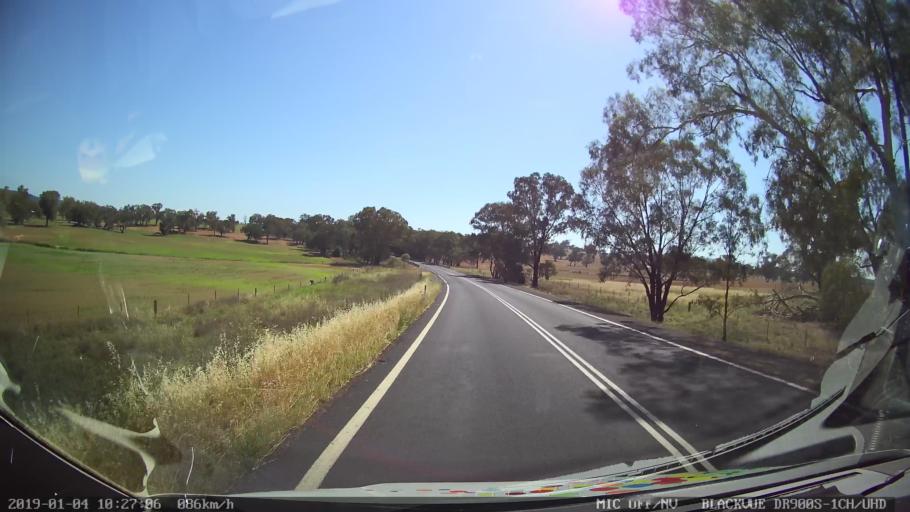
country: AU
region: New South Wales
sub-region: Cabonne
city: Canowindra
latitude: -33.3735
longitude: 148.5951
